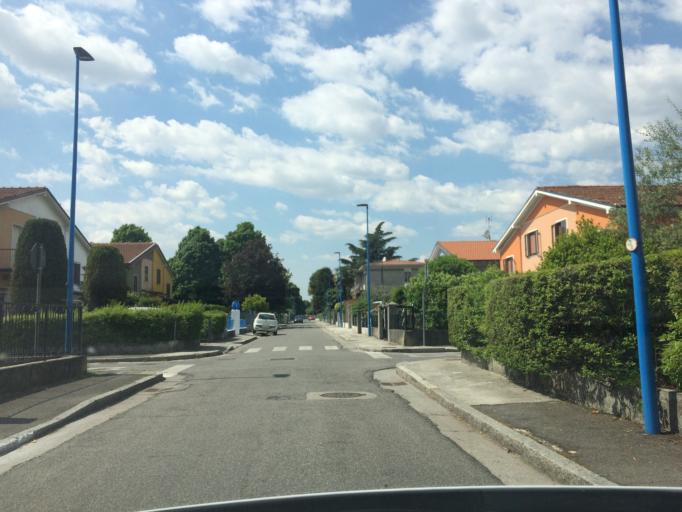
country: IT
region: Lombardy
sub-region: Provincia di Brescia
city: Folzano
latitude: 45.5090
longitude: 10.1898
